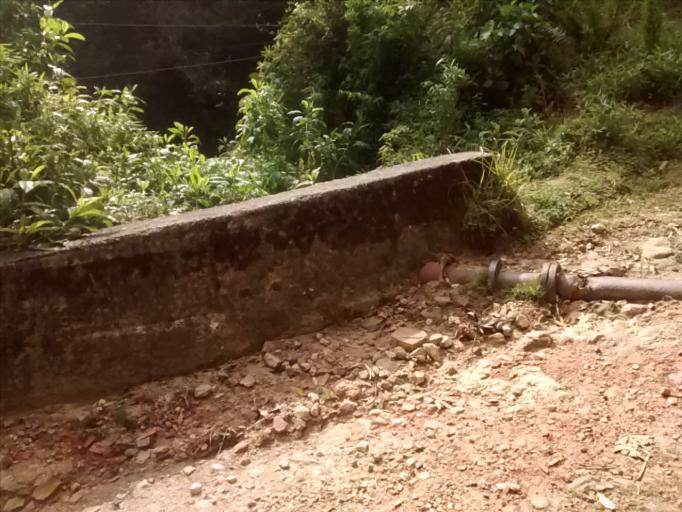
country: CO
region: Bogota D.C.
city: Bogota
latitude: 4.5574
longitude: -74.0624
